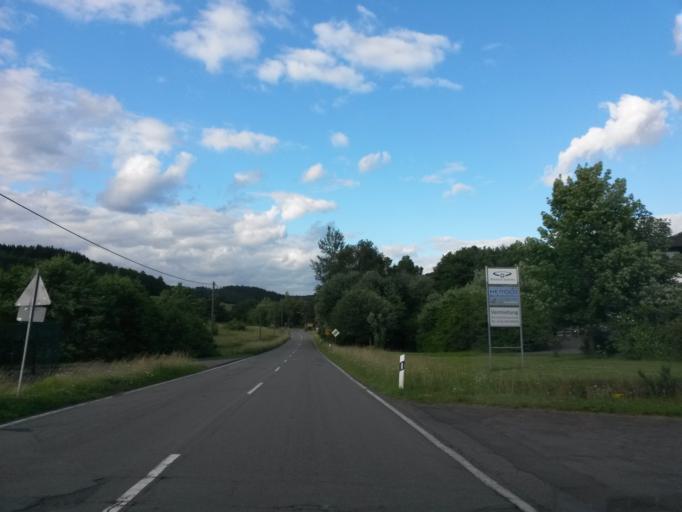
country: DE
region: North Rhine-Westphalia
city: Meinerzhagen
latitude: 51.0727
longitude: 7.7079
